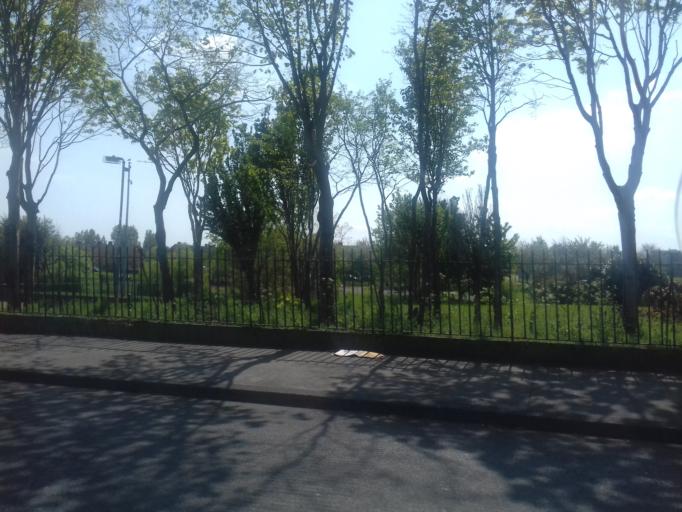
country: IE
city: Bonnybrook
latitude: 53.3967
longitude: -6.2035
